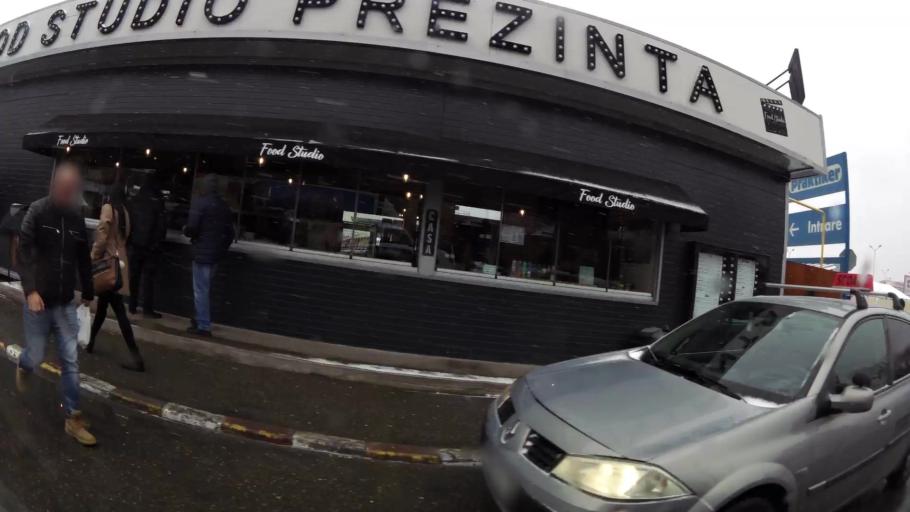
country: RO
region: Dambovita
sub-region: Municipiul Targoviste
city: Targoviste
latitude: 44.9223
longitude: 25.4643
